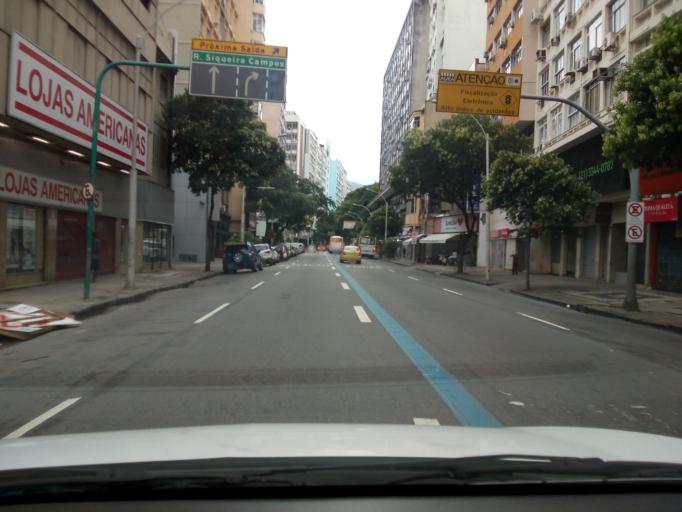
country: BR
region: Rio de Janeiro
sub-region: Rio De Janeiro
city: Rio de Janeiro
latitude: -22.9702
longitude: -43.1858
